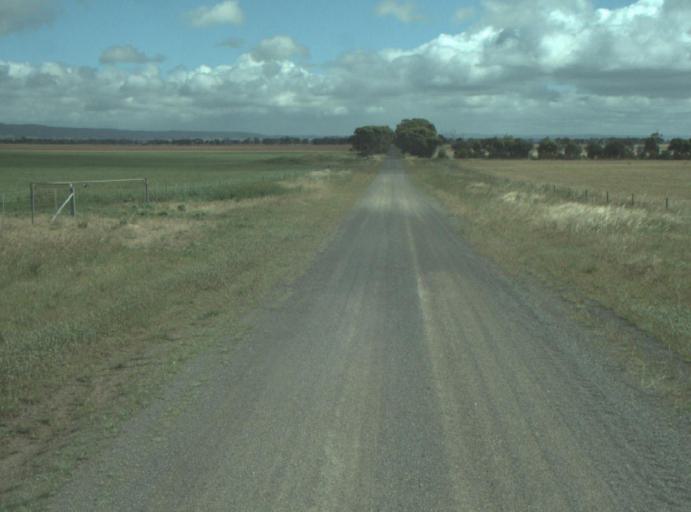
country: AU
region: Victoria
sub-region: Greater Geelong
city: Lara
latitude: -37.8867
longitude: 144.3502
